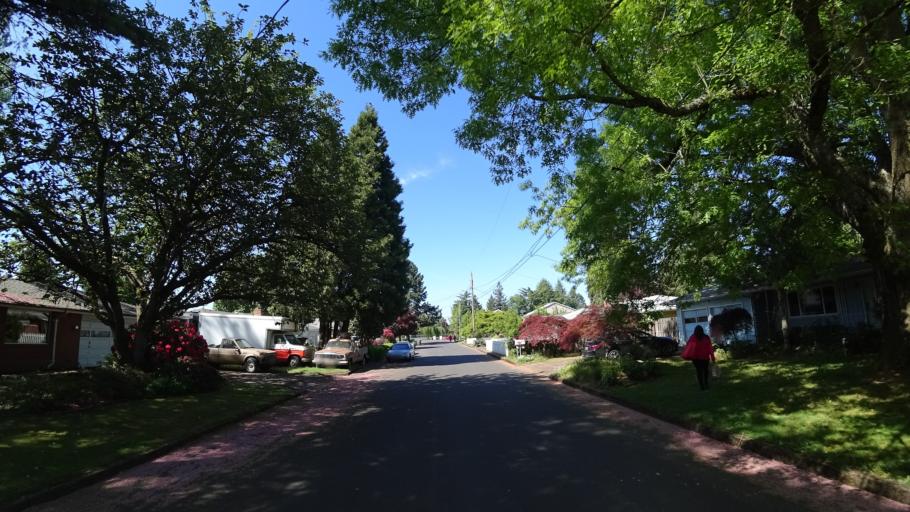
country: US
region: Oregon
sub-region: Washington County
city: Hillsboro
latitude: 45.5164
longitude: -122.9713
